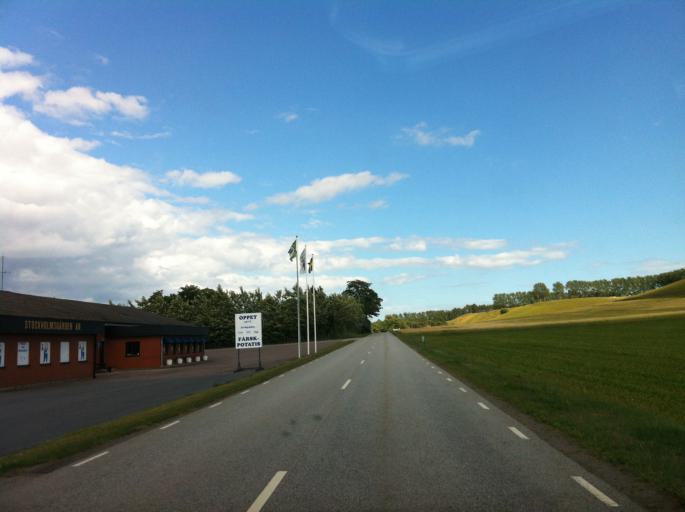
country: SE
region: Skane
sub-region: Ystads Kommun
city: Kopingebro
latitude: 55.4121
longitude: 14.0149
